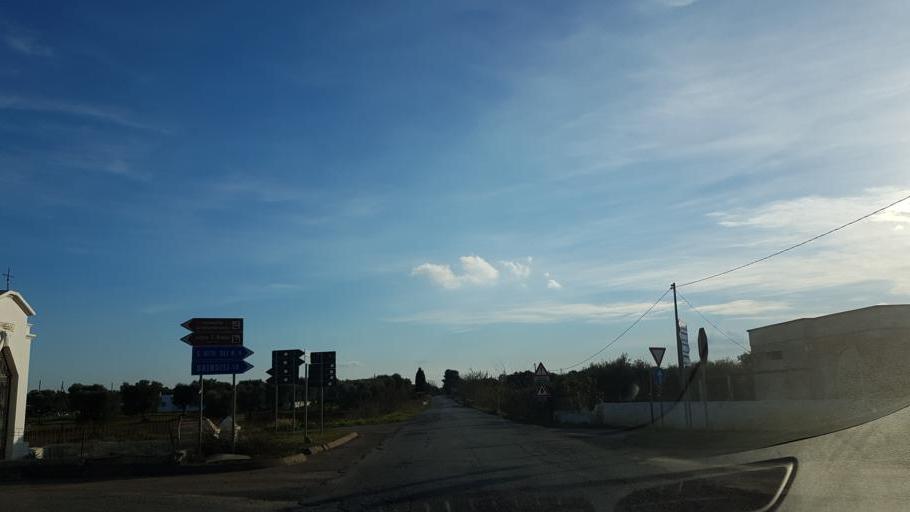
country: IT
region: Apulia
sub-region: Provincia di Brindisi
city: San Vito dei Normanni
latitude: 40.6649
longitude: 17.7793
